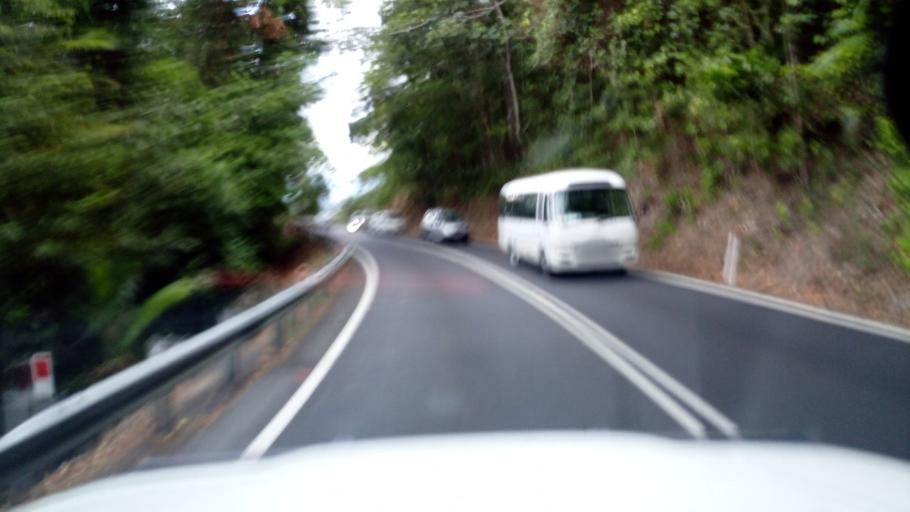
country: AU
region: Queensland
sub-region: Tablelands
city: Kuranda
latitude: -16.8357
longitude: 145.6716
